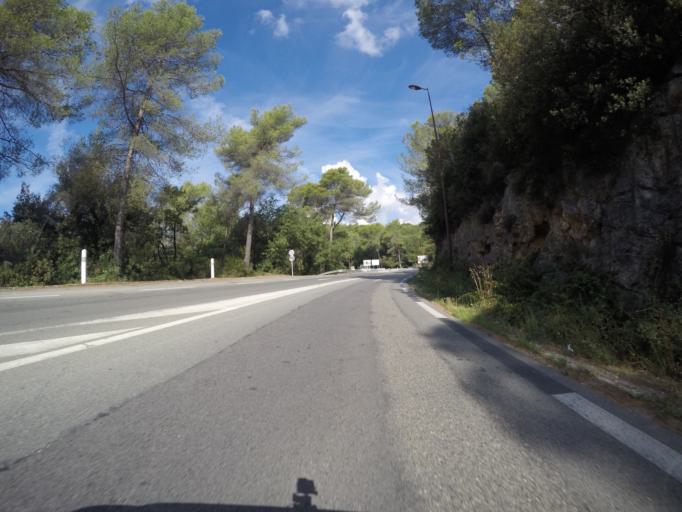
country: FR
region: Provence-Alpes-Cote d'Azur
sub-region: Departement des Alpes-Maritimes
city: Le Rouret
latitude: 43.6717
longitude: 7.0288
